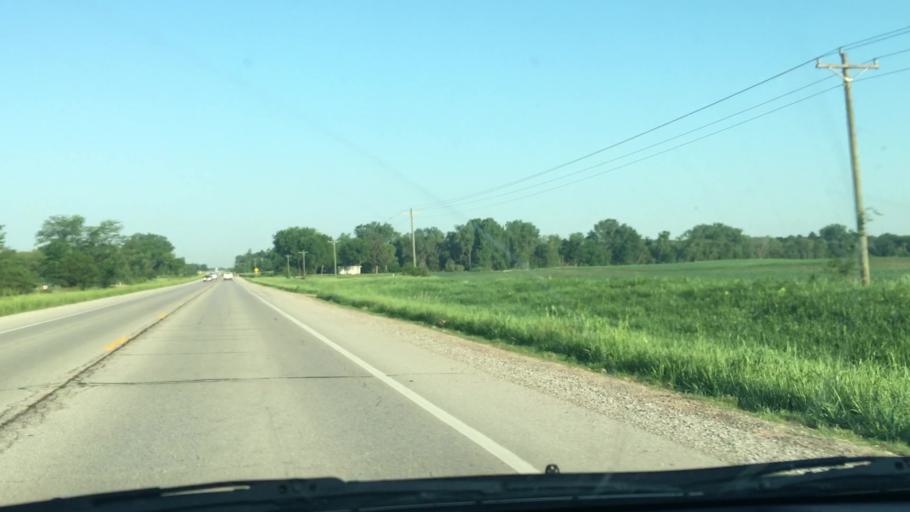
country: US
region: Iowa
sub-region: Johnson County
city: Tiffin
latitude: 41.7137
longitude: -91.7062
